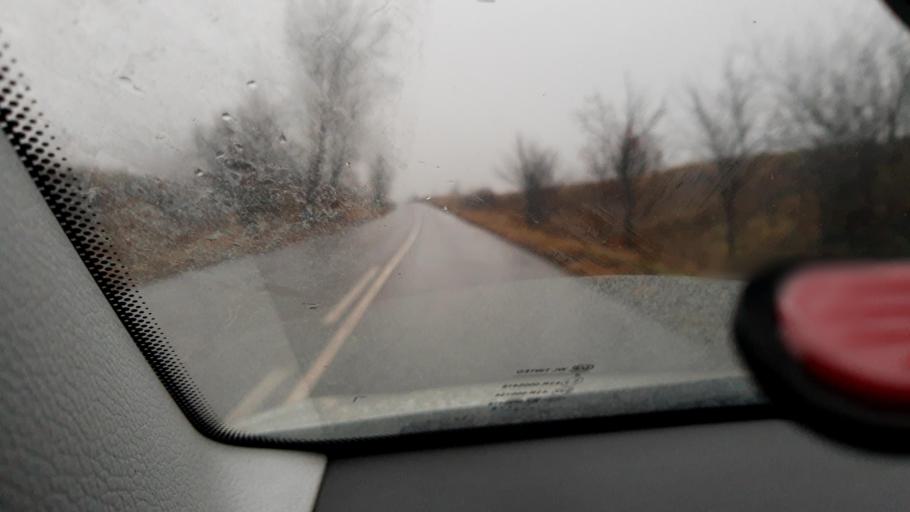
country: RU
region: Bashkortostan
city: Iglino
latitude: 54.8996
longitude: 56.2157
